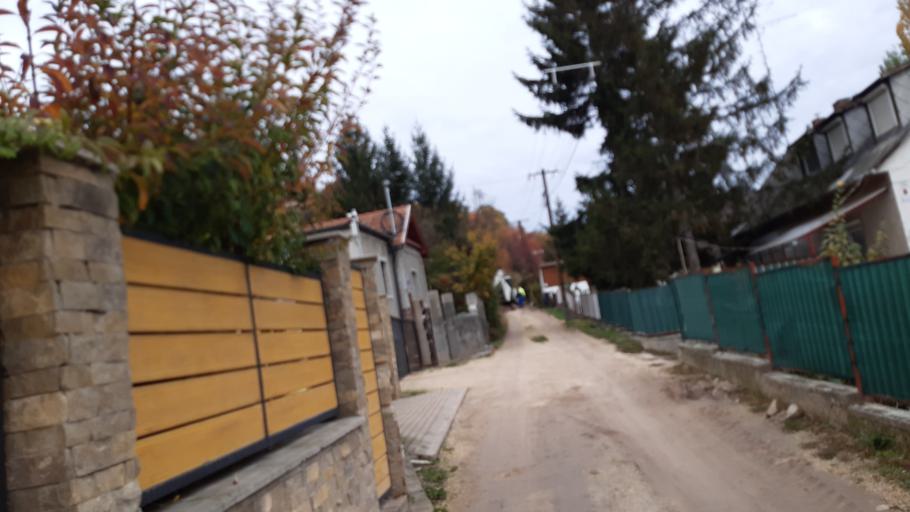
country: HU
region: Veszprem
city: Balatonalmadi
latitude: 47.0450
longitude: 18.0028
